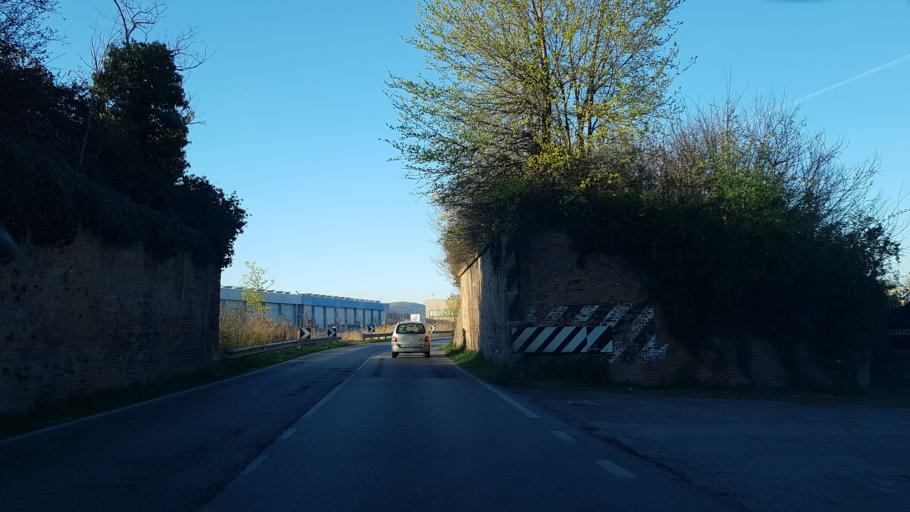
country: IT
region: Veneto
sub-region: Provincia di Vicenza
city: Ponte di Nanto
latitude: 45.4124
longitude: 11.5850
